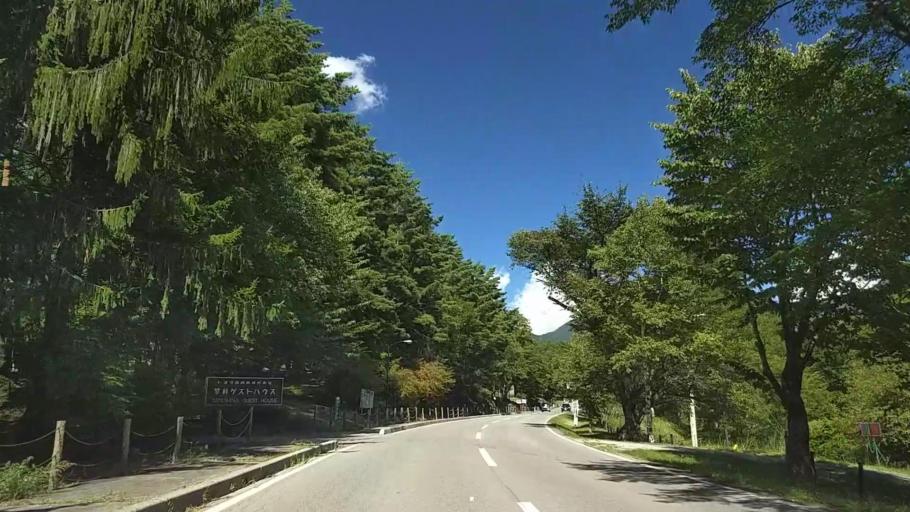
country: JP
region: Nagano
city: Chino
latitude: 36.0488
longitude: 138.2501
